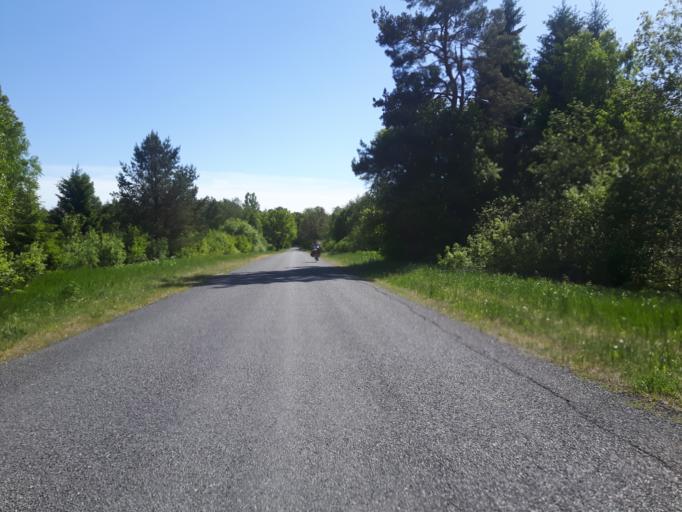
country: EE
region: Laeaene-Virumaa
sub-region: Haljala vald
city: Haljala
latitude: 59.5439
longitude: 26.2366
